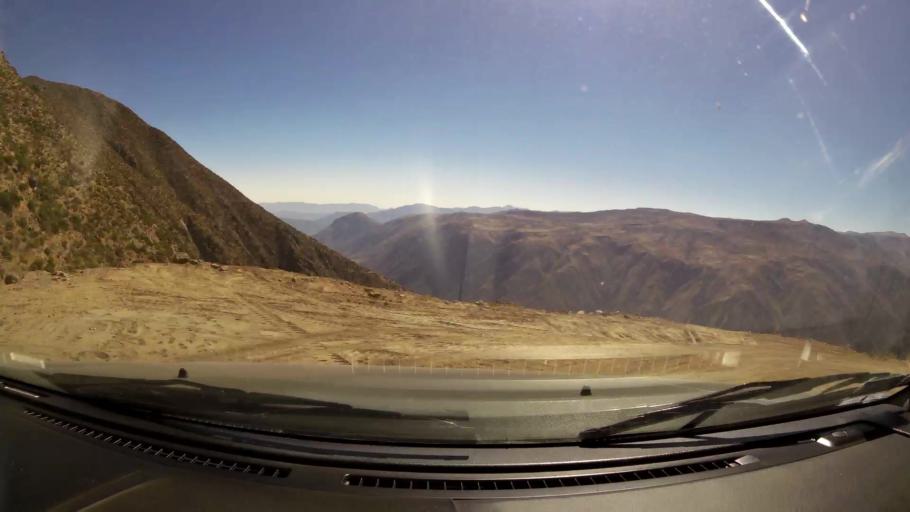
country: PE
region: Huancavelica
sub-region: Huaytara
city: Quito-Arma
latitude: -13.6208
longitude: -75.3535
